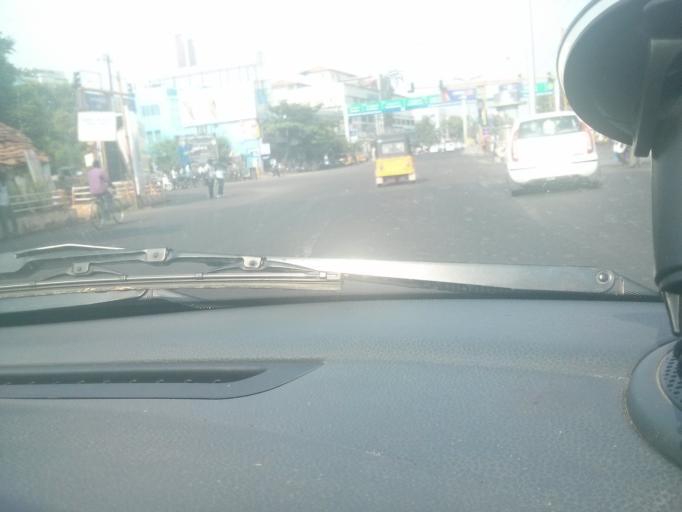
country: IN
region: Tamil Nadu
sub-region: Coimbatore
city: Coimbatore
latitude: 11.0131
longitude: 76.9863
